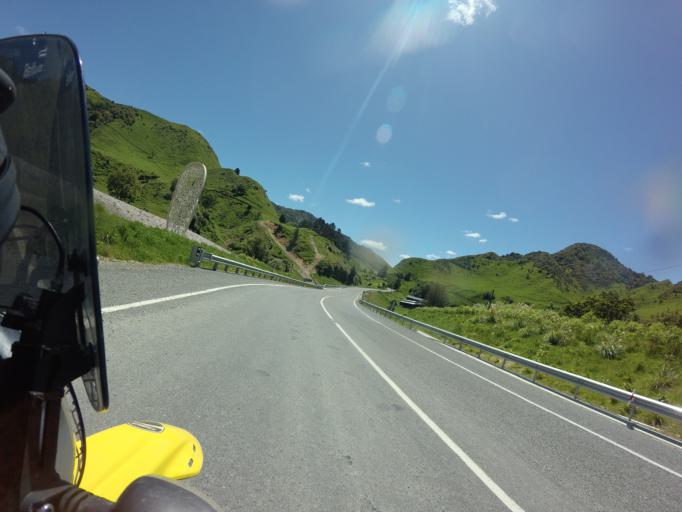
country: NZ
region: Bay of Plenty
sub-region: Opotiki District
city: Opotiki
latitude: -38.3806
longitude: 177.4703
